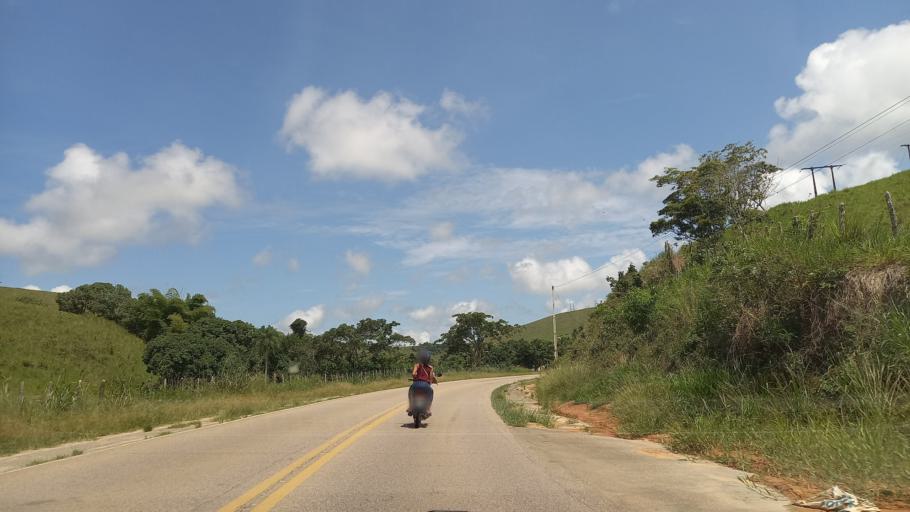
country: BR
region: Pernambuco
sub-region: Tamandare
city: Tamandare
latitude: -8.7481
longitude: -35.1710
